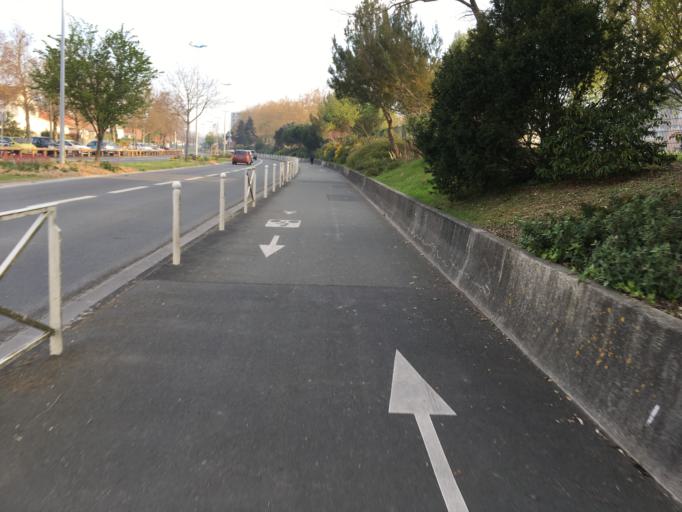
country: FR
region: Poitou-Charentes
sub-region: Departement de la Charente-Maritime
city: La Rochelle
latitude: 46.1741
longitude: -1.1503
